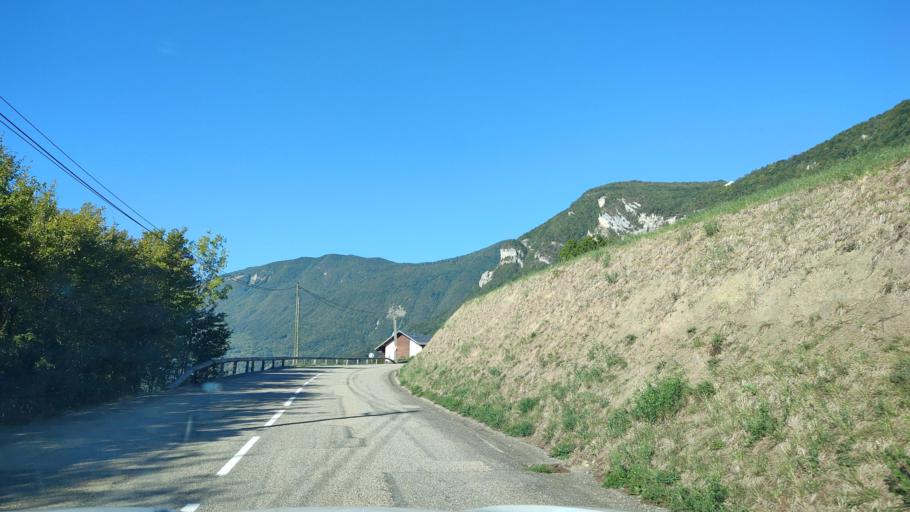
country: FR
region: Rhone-Alpes
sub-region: Departement de la Savoie
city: Coise-Saint-Jean-Pied-Gauthier
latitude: 45.5754
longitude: 6.1531
